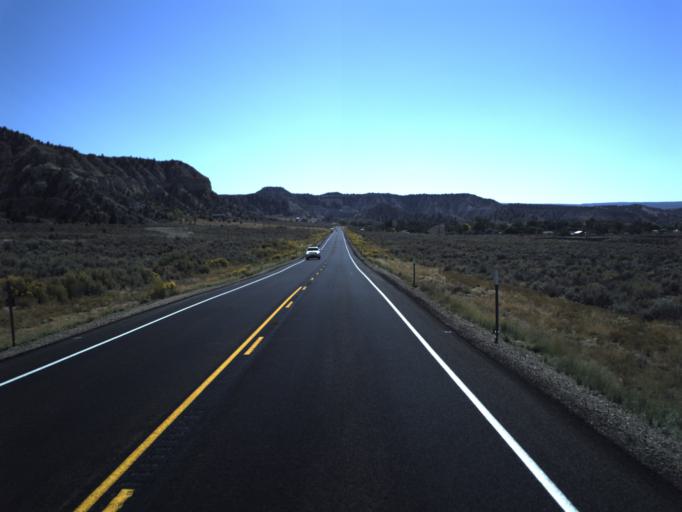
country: US
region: Utah
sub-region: Garfield County
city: Panguitch
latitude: 37.5756
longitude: -111.9872
